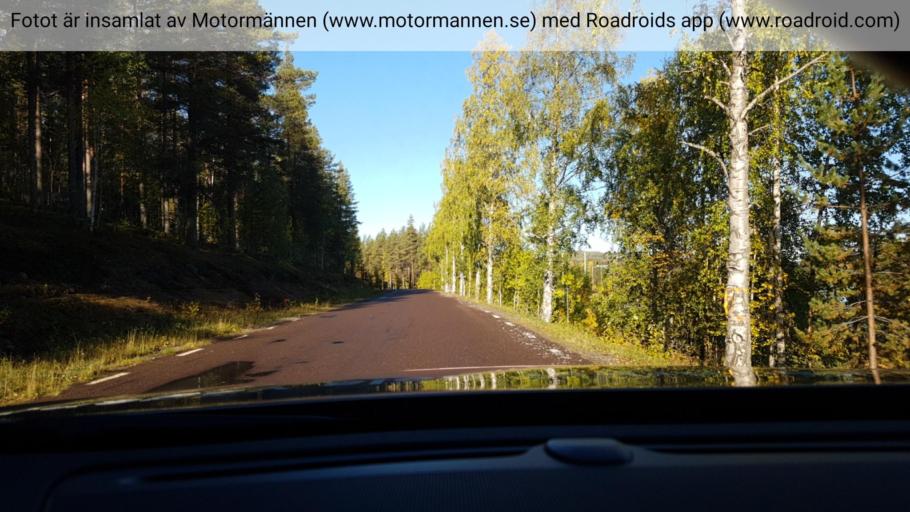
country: SE
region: Norrbotten
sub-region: Bodens Kommun
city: Boden
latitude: 66.1312
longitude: 21.3048
